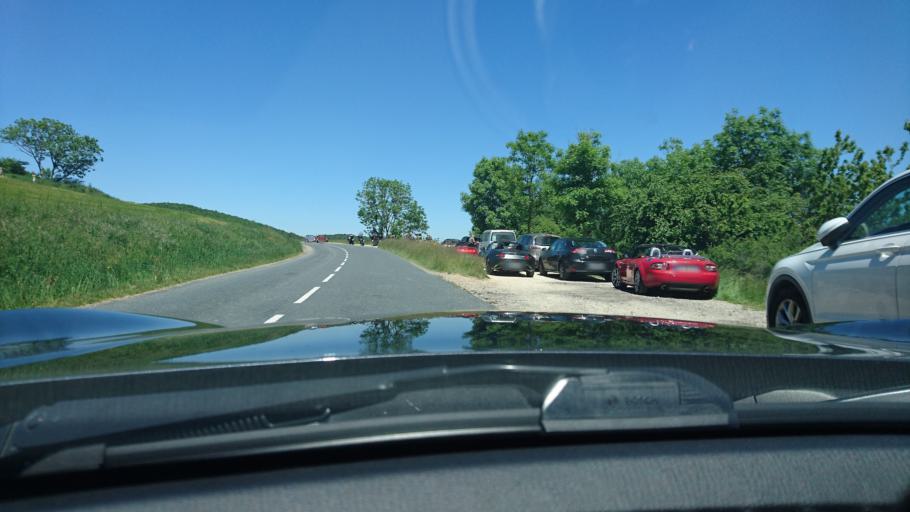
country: FR
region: Rhone-Alpes
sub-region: Departement du Rhone
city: Courzieu
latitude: 45.7252
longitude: 4.5996
